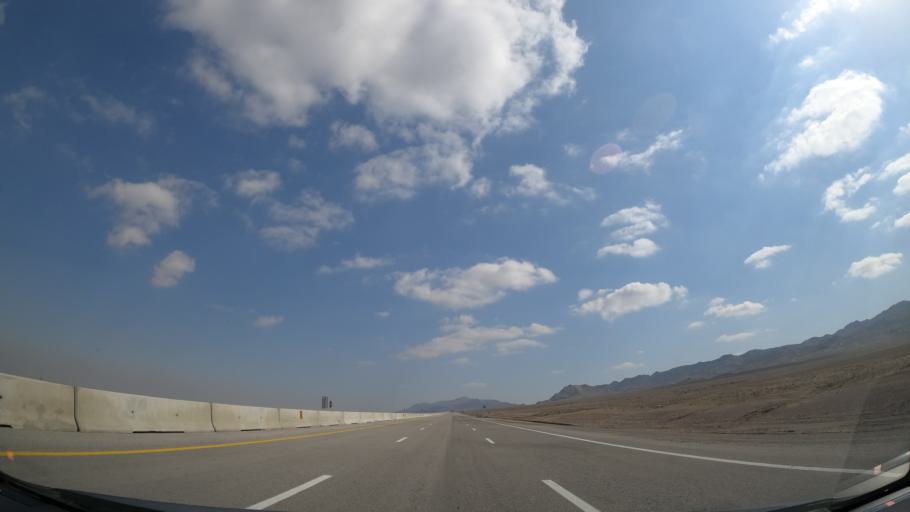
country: IR
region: Alborz
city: Eshtehard
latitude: 35.7141
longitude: 50.5853
